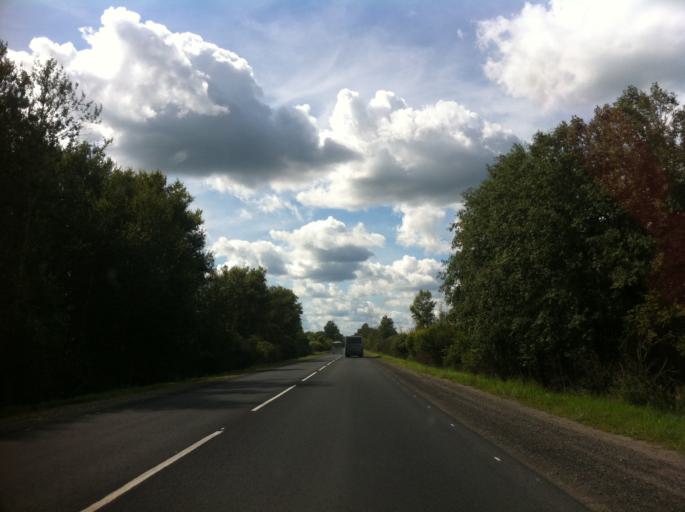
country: RU
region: Pskov
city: Izborsk
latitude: 57.7269
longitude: 27.9585
